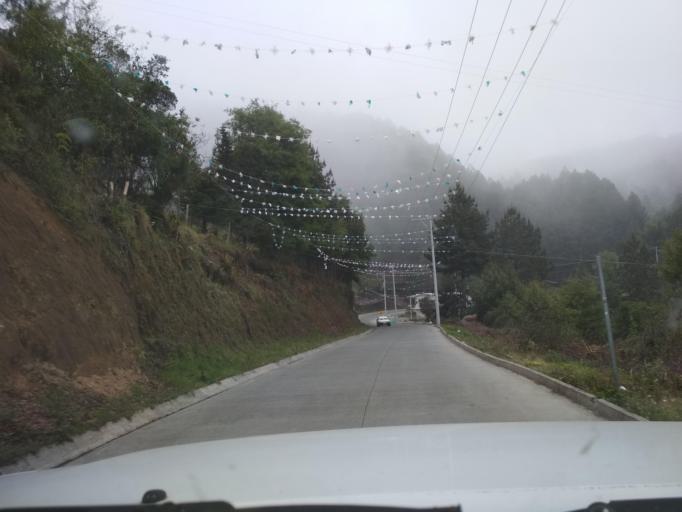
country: MX
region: Veracruz
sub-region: La Perla
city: Chilapa
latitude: 18.9768
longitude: -97.1900
